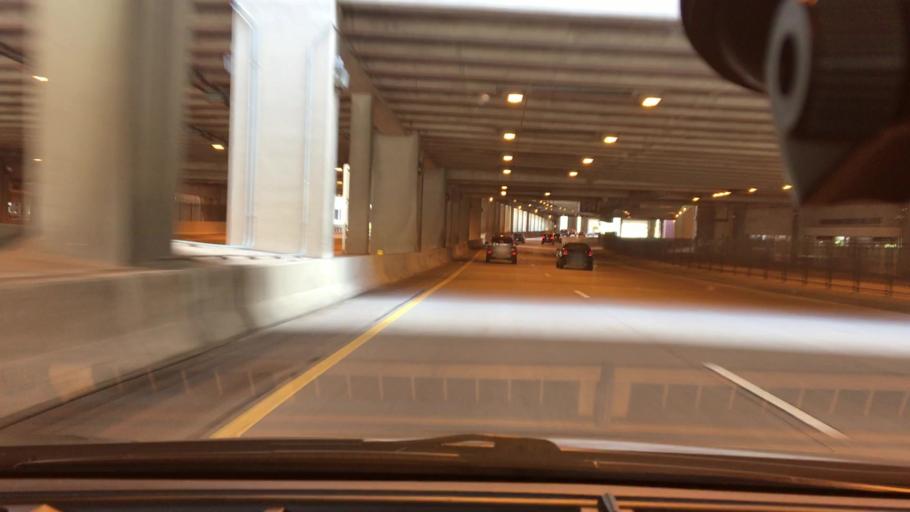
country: US
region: Minnesota
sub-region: Hennepin County
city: Minneapolis
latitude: 44.9817
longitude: -93.2755
